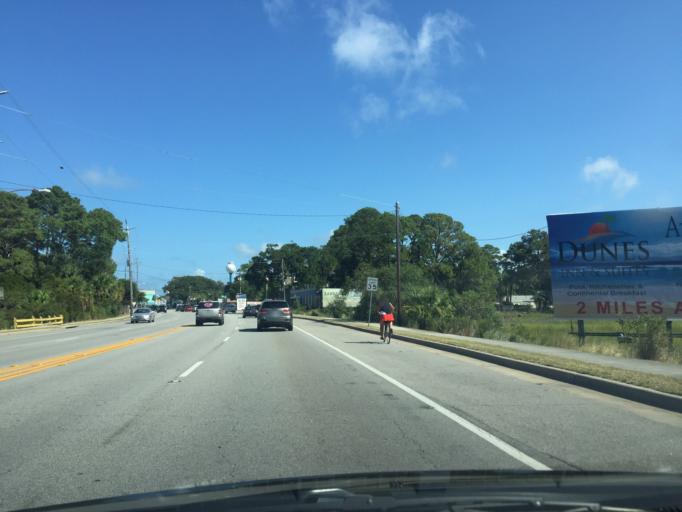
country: US
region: Georgia
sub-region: Chatham County
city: Tybee Island
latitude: 32.0148
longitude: -80.8477
